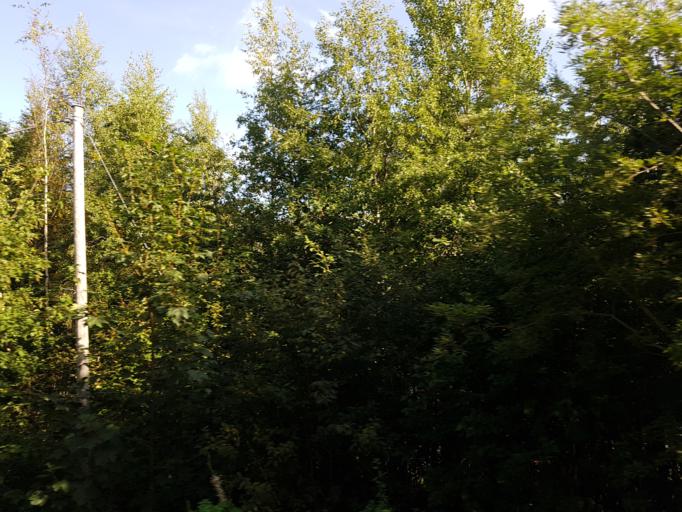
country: NO
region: Sor-Trondelag
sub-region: Afjord
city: Arnes
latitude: 63.9685
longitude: 10.2237
